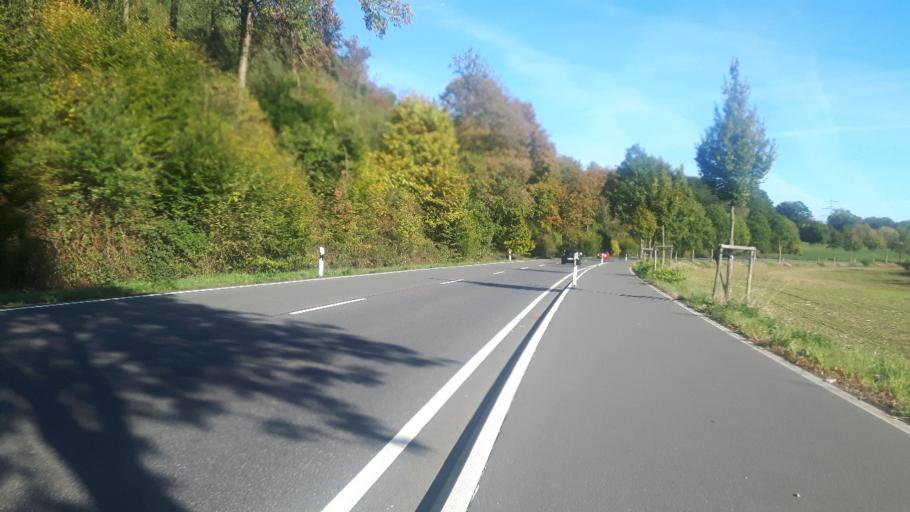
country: DE
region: Rheinland-Pfalz
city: Katzwinkel
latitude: 50.8052
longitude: 7.7939
